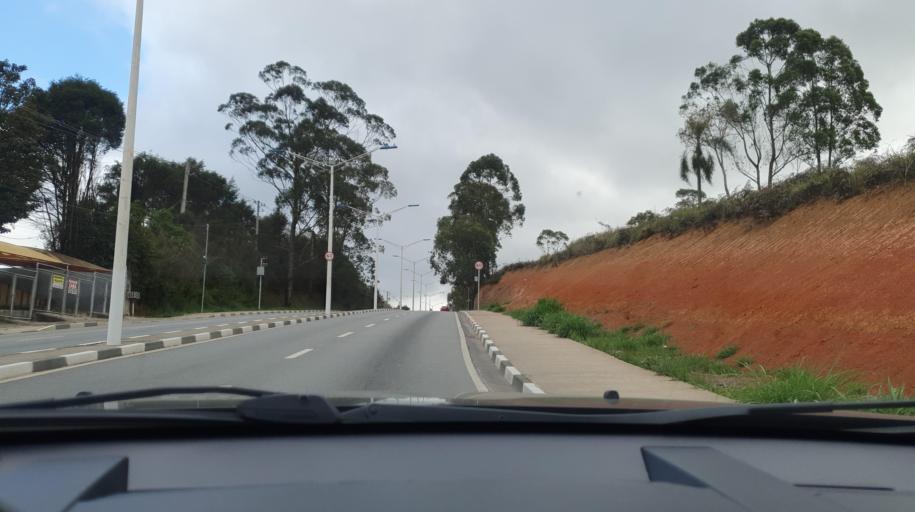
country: BR
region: Sao Paulo
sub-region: Vargem Grande Paulista
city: Vargem Grande Paulista
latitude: -23.6631
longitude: -47.0081
